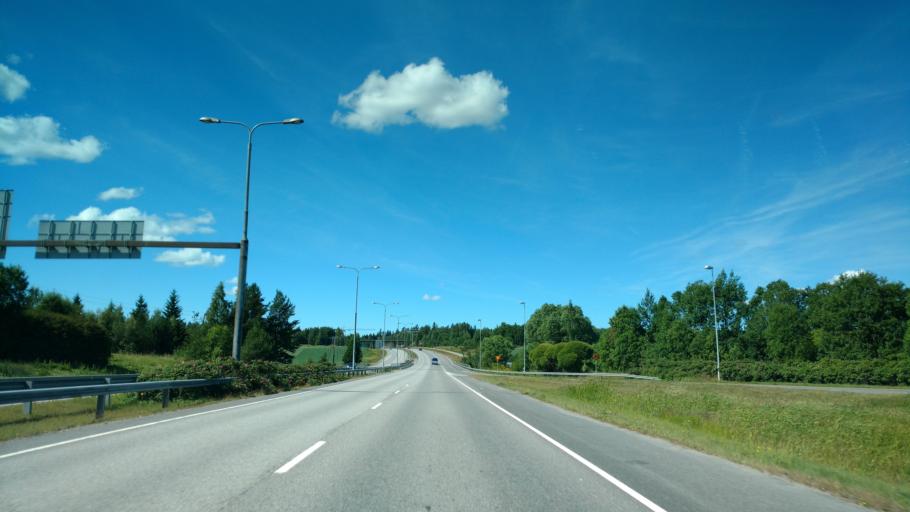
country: FI
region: Varsinais-Suomi
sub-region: Turku
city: Turku
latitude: 60.4878
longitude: 22.3190
